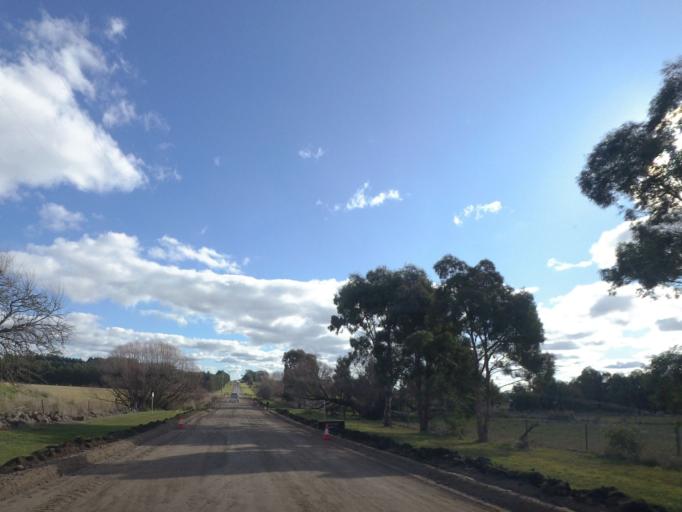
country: AU
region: Victoria
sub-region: Mount Alexander
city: Castlemaine
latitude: -37.2547
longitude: 144.4295
